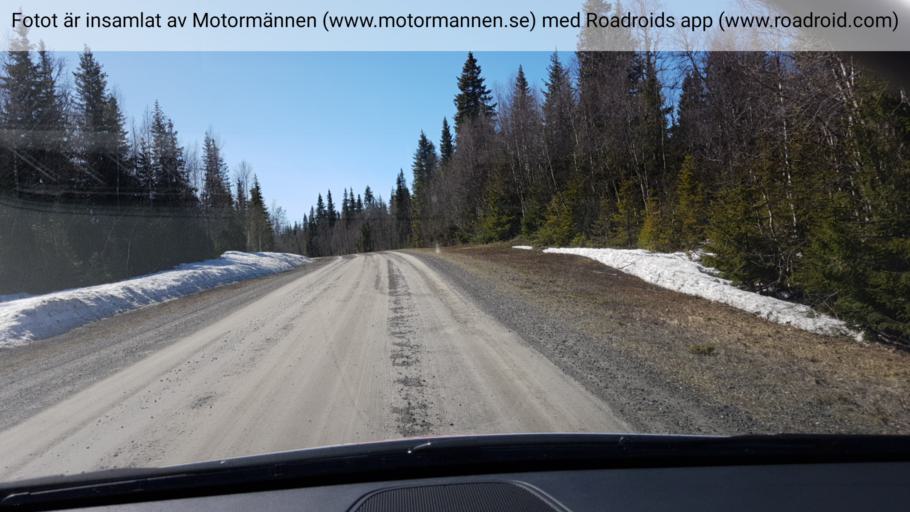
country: NO
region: Nord-Trondelag
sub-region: Snasa
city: Snaase
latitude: 63.7116
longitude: 12.4271
